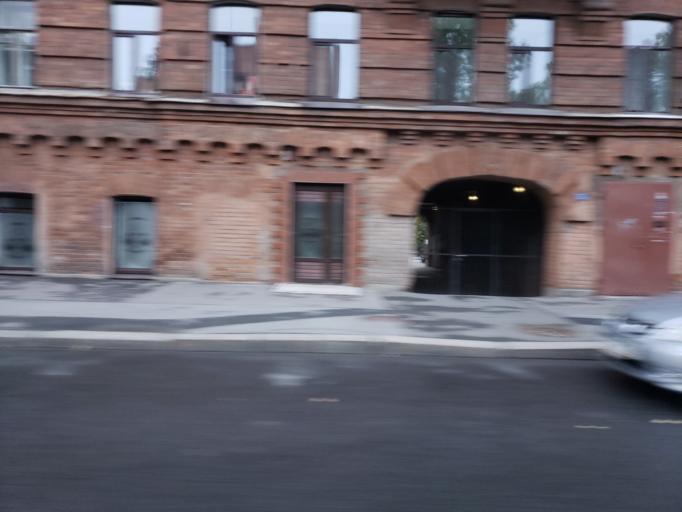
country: RU
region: St.-Petersburg
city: Vasyl'evsky Ostrov
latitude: 59.9301
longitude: 30.2523
